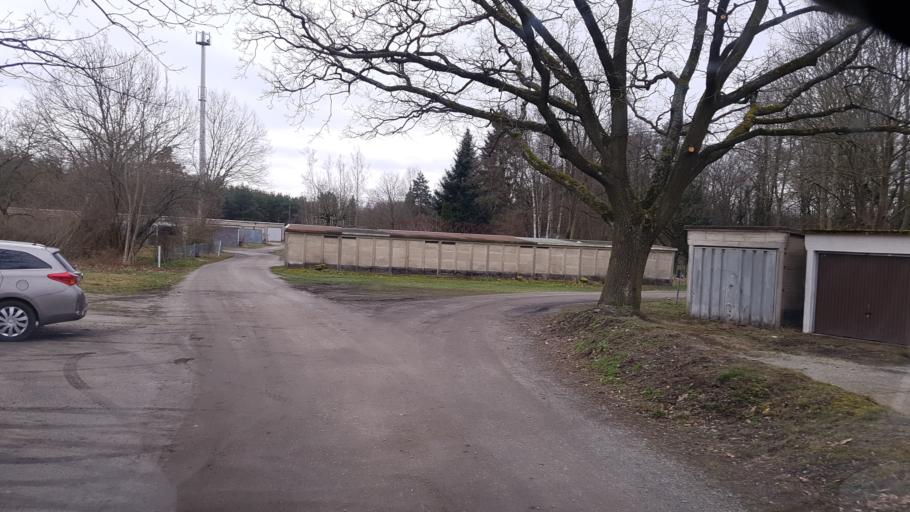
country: DE
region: Brandenburg
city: Ruhland
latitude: 51.4520
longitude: 13.8577
